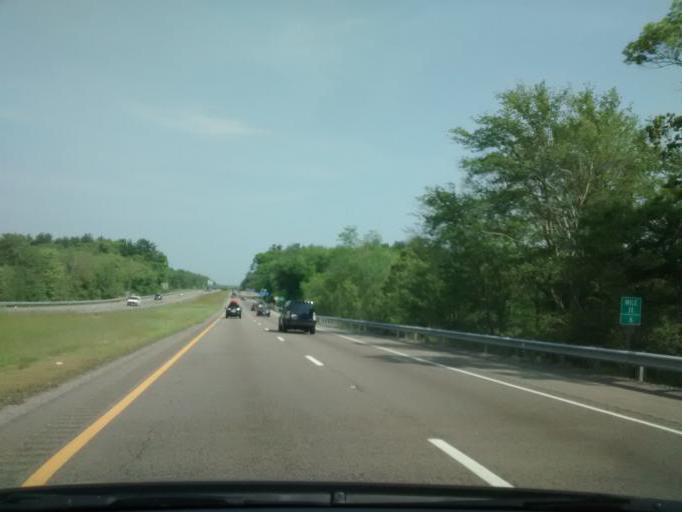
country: US
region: Massachusetts
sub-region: Plymouth County
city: Middleborough Center
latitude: 41.8791
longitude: -70.9133
